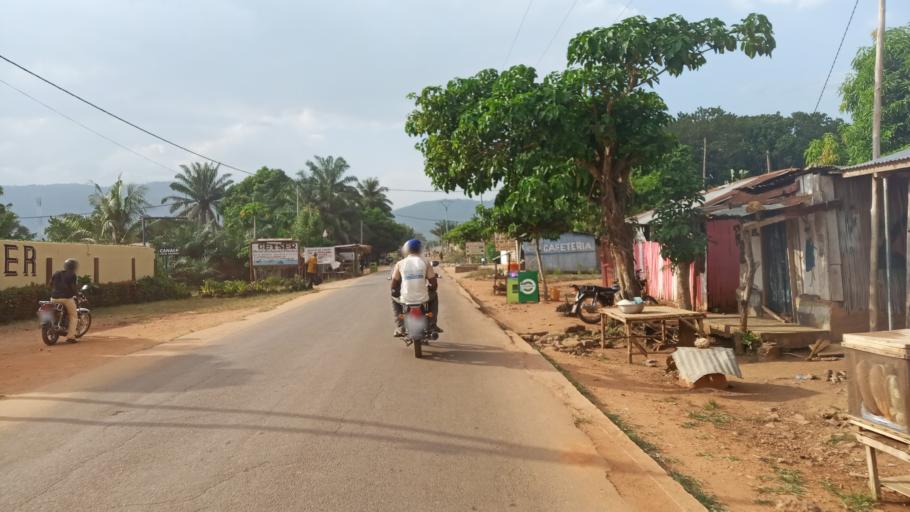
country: TG
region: Plateaux
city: Kpalime
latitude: 6.9211
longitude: 0.6200
